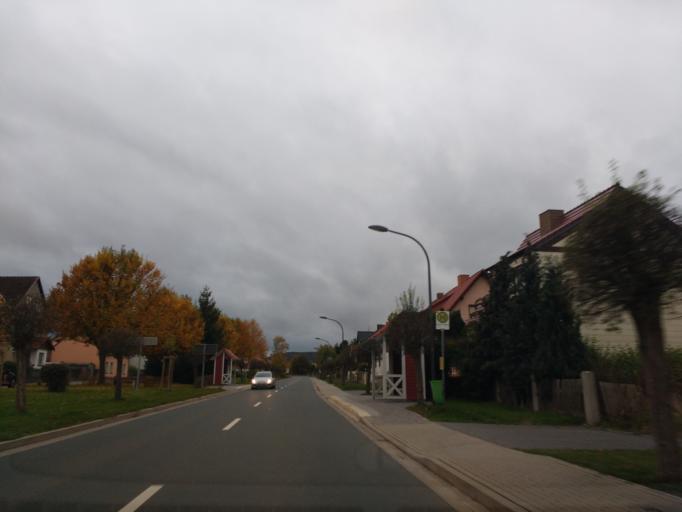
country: DE
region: Thuringia
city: Grossbodungen
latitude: 51.4763
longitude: 10.4780
